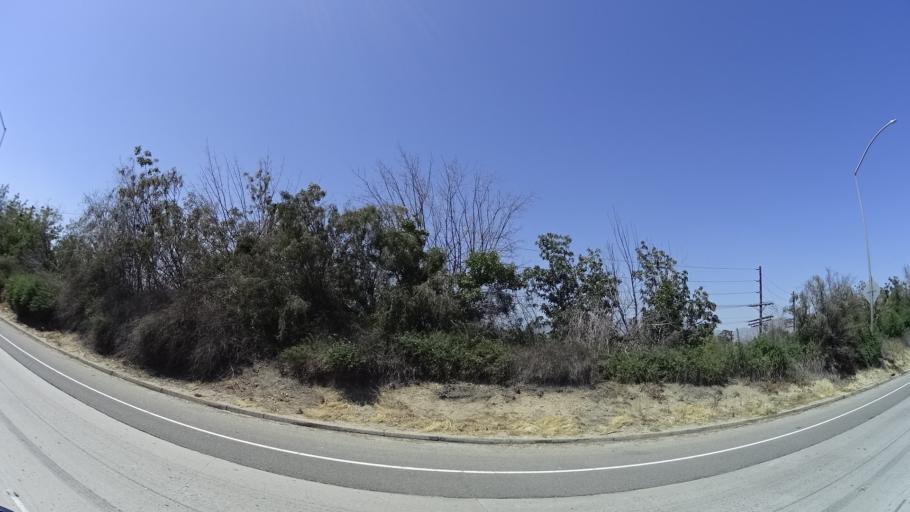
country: US
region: California
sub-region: Los Angeles County
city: San Fernando
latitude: 34.2665
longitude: -118.4470
